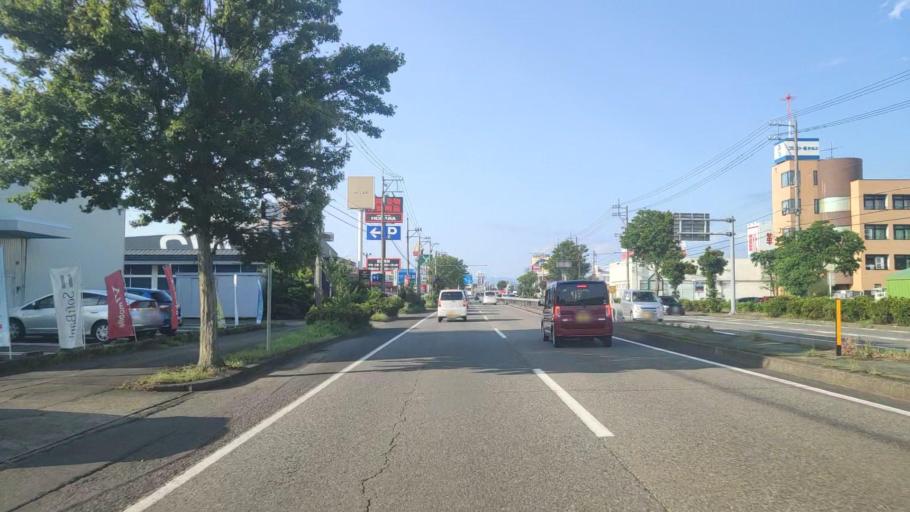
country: JP
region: Fukui
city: Fukui-shi
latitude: 36.0386
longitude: 136.2302
